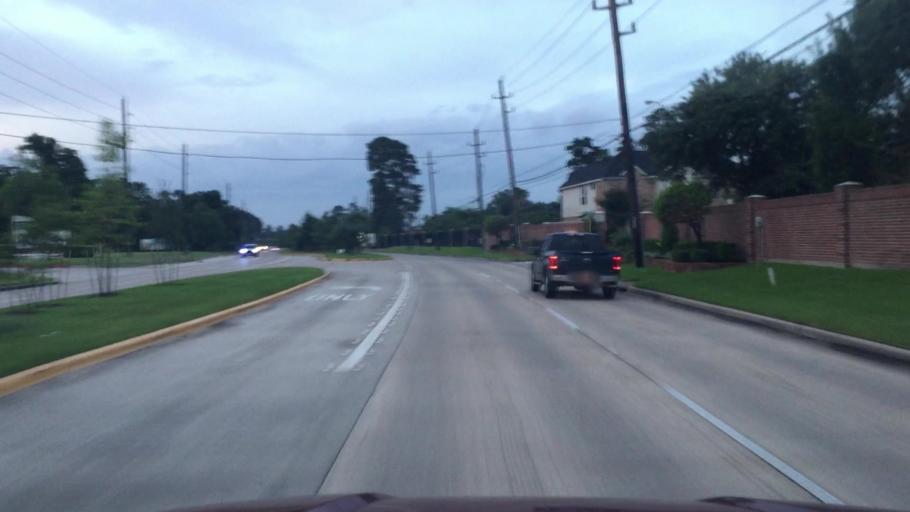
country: US
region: Texas
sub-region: Harris County
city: Tomball
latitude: 30.0349
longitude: -95.5355
